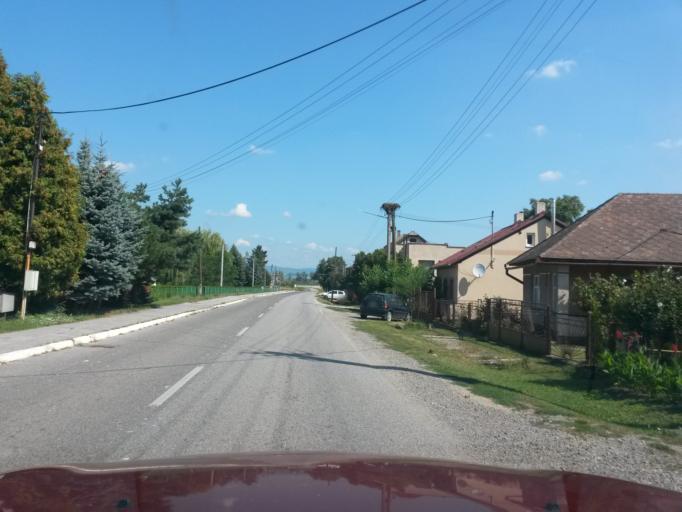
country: SK
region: Kosicky
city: Moldava nad Bodvou
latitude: 48.5355
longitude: 21.0778
